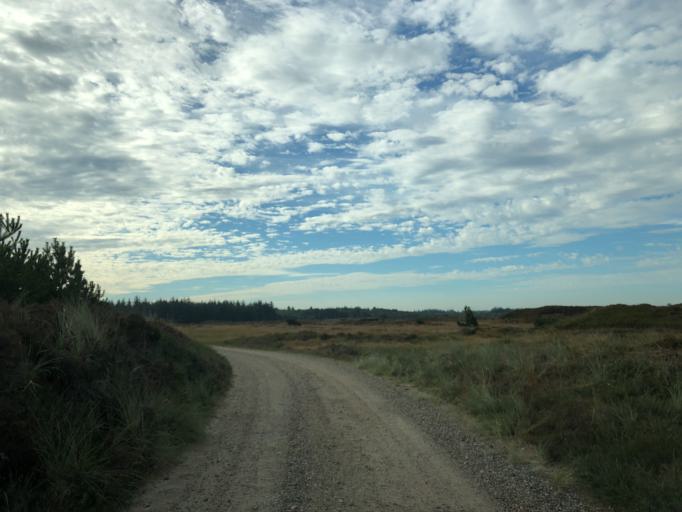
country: DK
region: Central Jutland
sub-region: Holstebro Kommune
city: Ulfborg
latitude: 56.1824
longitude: 8.3491
